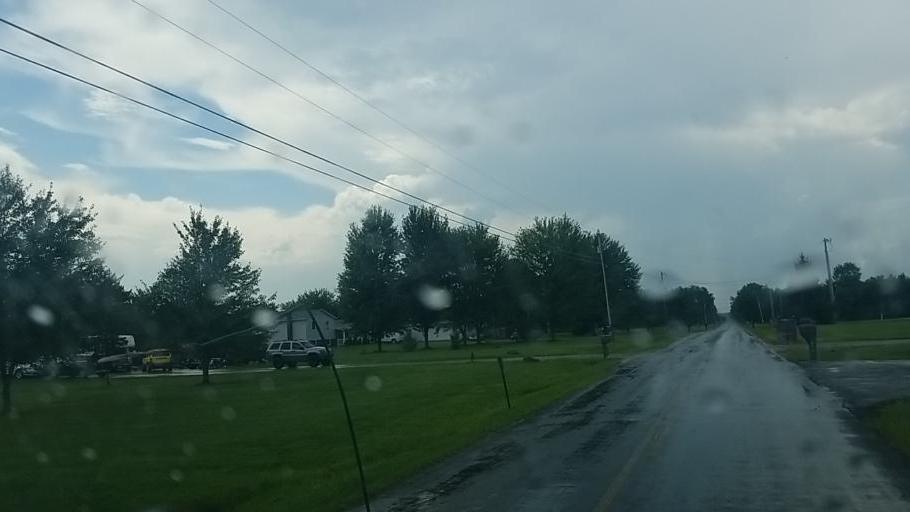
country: US
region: Ohio
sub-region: Lorain County
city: Grafton
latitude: 41.1583
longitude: -82.0279
